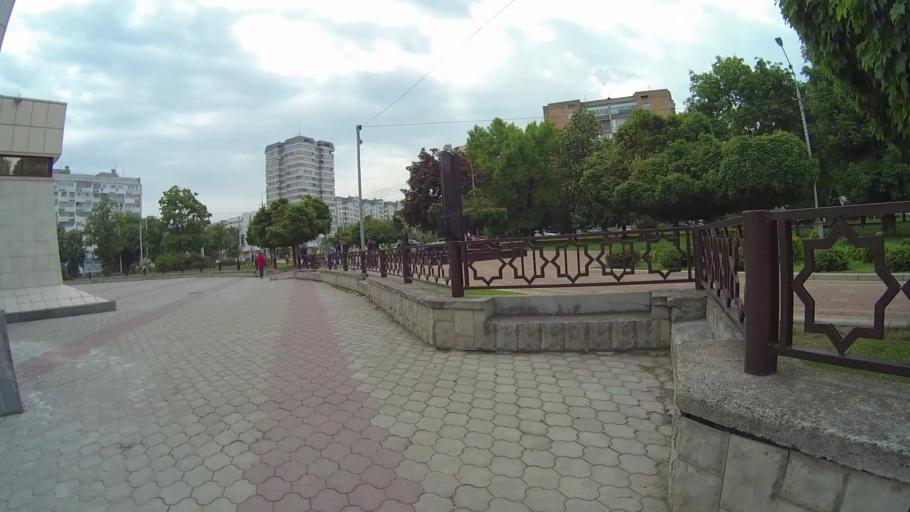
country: RU
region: Kabardino-Balkariya
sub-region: Gorod Nal'chik
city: Nal'chik
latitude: 43.4886
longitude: 43.6165
